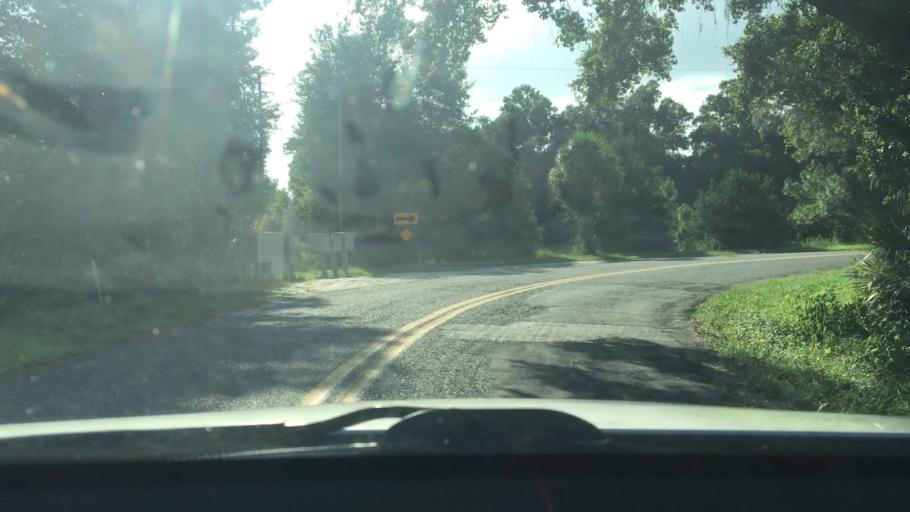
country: US
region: Florida
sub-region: Volusia County
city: Lake Helen
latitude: 28.9636
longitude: -81.2148
